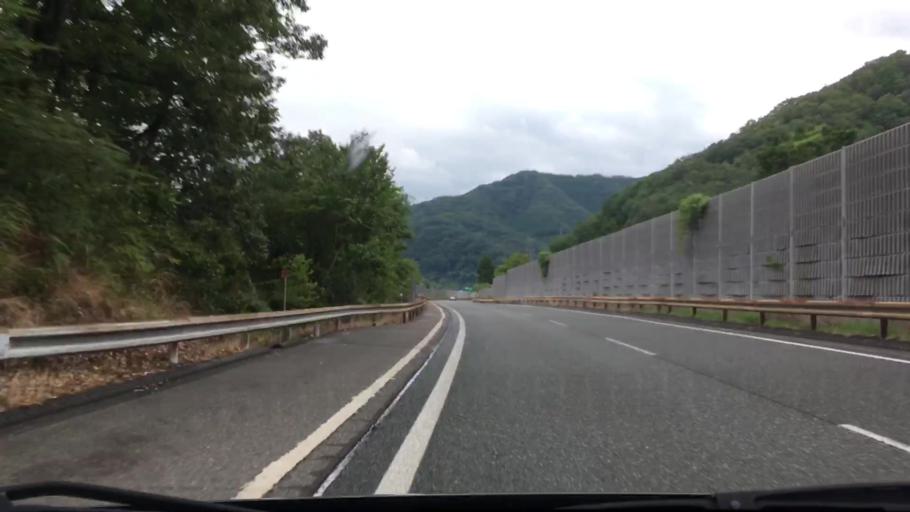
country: JP
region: Okayama
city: Niimi
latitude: 34.9954
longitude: 133.4679
